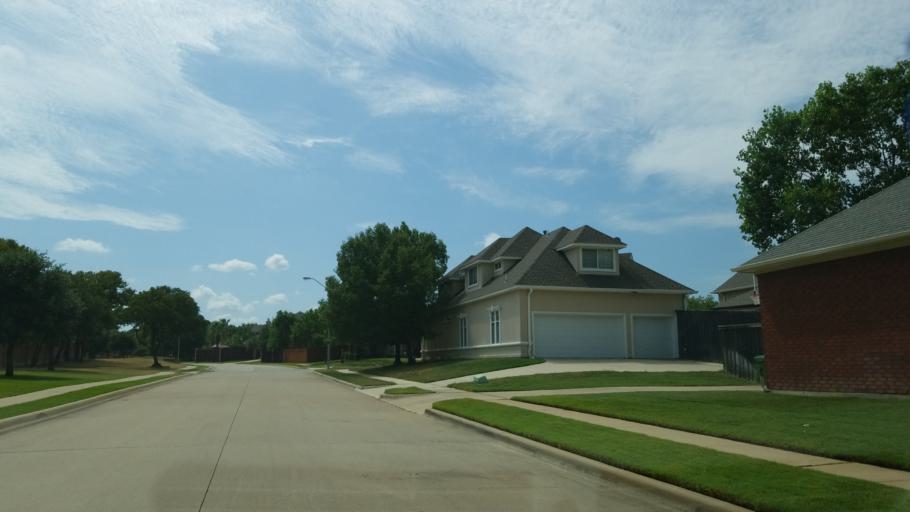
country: US
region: Texas
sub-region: Tarrant County
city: Grapevine
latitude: 32.8985
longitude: -97.1015
